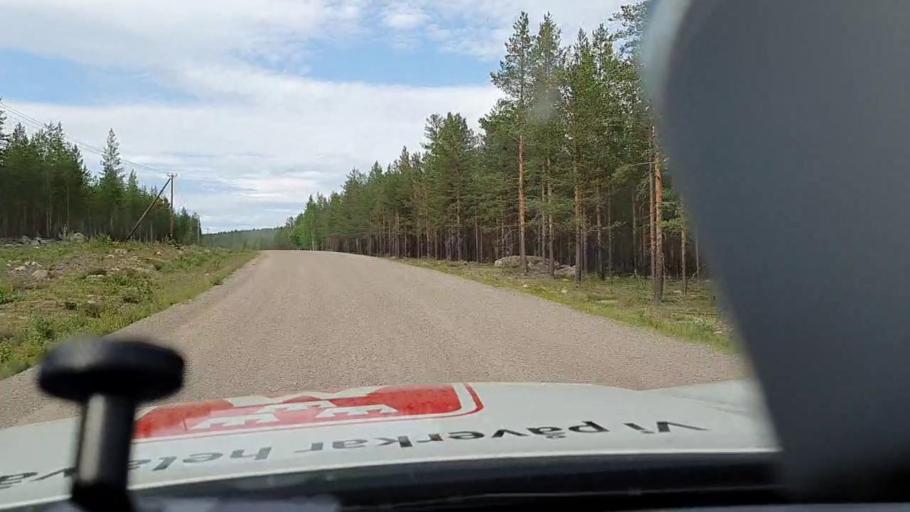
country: SE
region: Norrbotten
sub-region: Alvsbyns Kommun
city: AElvsbyn
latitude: 66.1228
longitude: 20.9930
